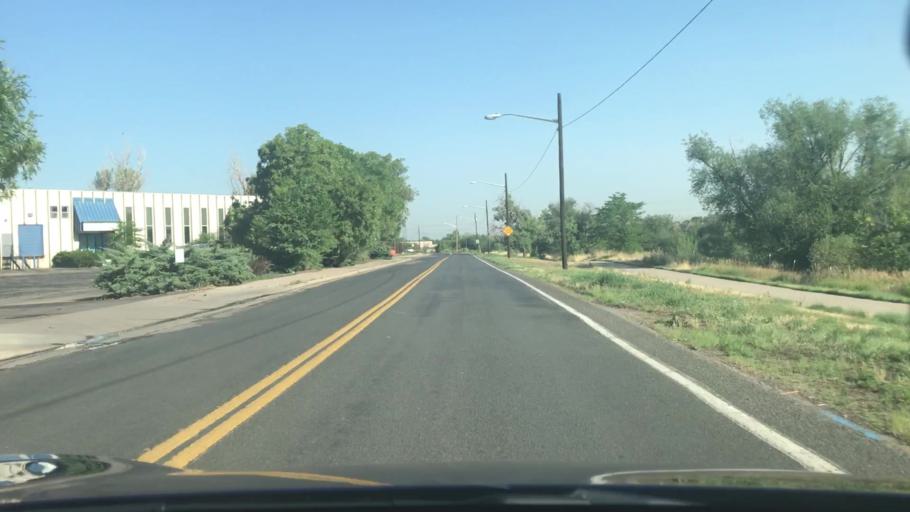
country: US
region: Colorado
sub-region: Arapahoe County
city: Glendale
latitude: 39.6813
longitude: -104.8984
